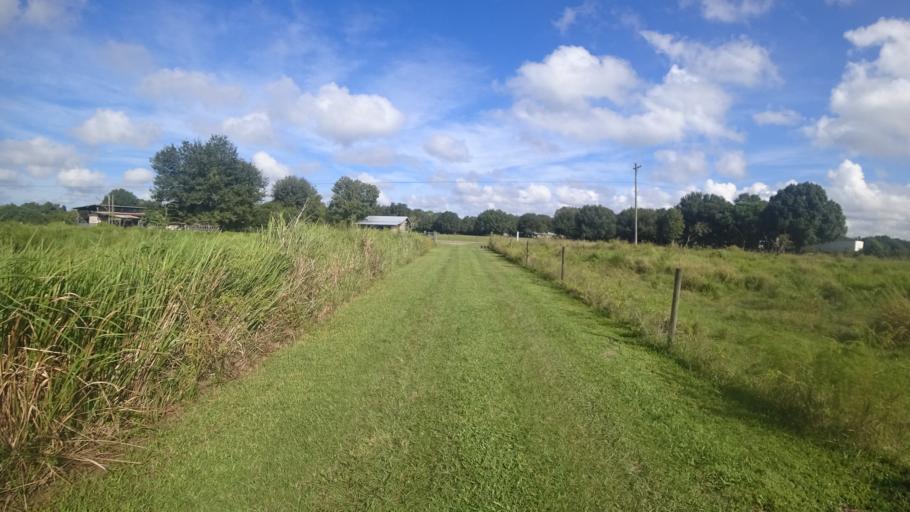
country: US
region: Florida
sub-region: Hillsborough County
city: Ruskin
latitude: 27.6118
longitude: -82.3975
